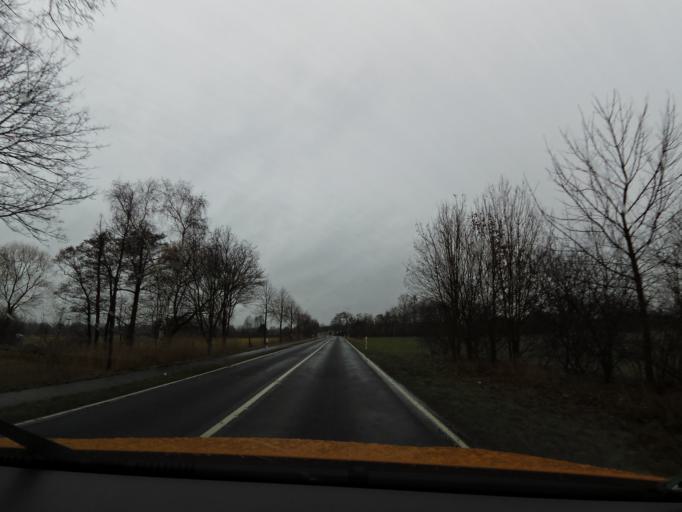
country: DE
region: Brandenburg
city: Zossen
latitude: 52.1996
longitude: 13.4316
